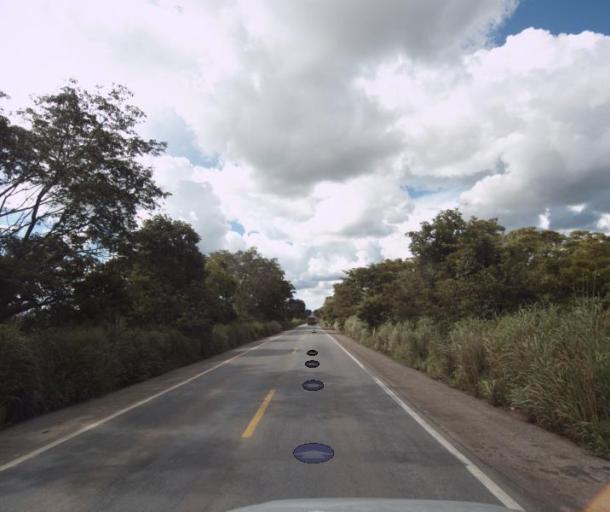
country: BR
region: Goias
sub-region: Porangatu
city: Porangatu
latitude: -13.3346
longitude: -49.1205
